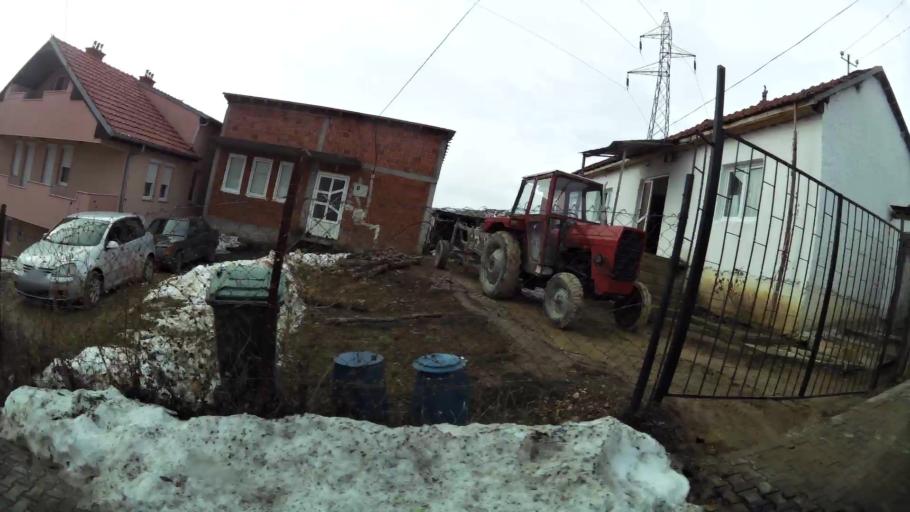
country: XK
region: Pristina
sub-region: Komuna e Prishtines
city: Pristina
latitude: 42.6888
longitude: 21.1744
